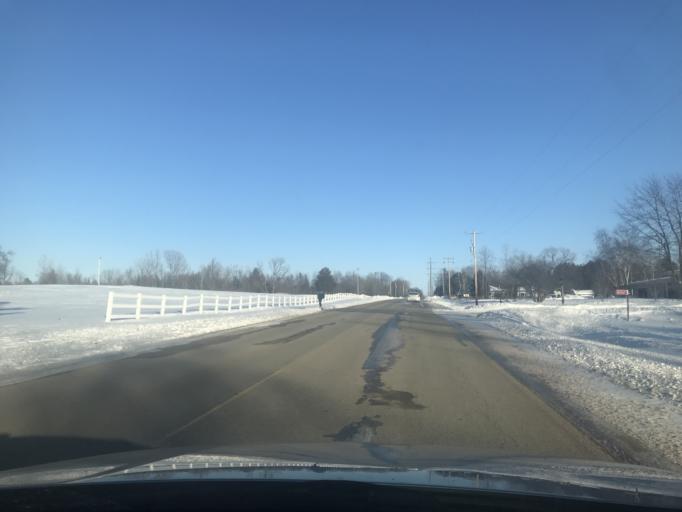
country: US
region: Wisconsin
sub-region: Marinette County
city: Marinette
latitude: 45.1451
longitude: -87.6569
